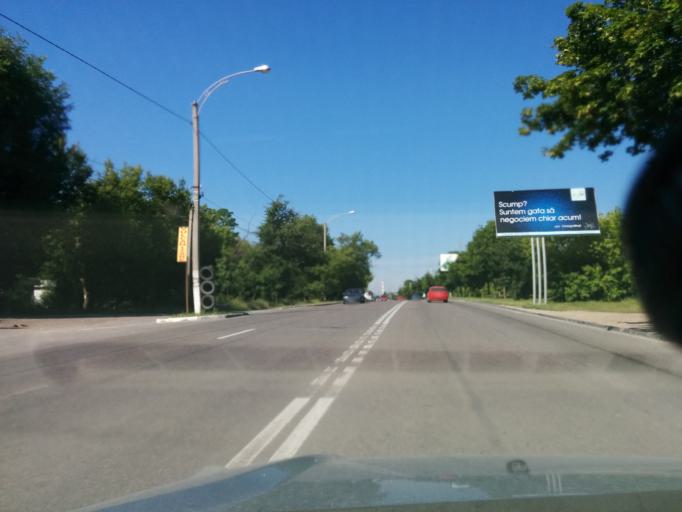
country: MD
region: Chisinau
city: Chisinau
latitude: 47.0350
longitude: 28.8945
